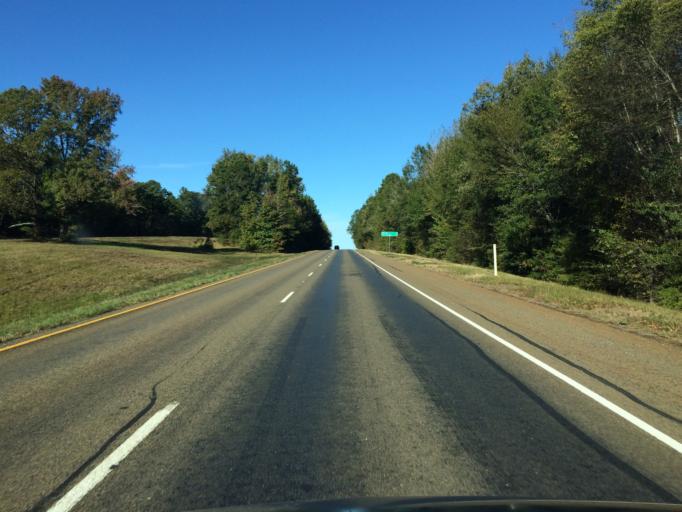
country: US
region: Texas
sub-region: Wood County
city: Hawkins
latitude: 32.5884
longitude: -95.2142
